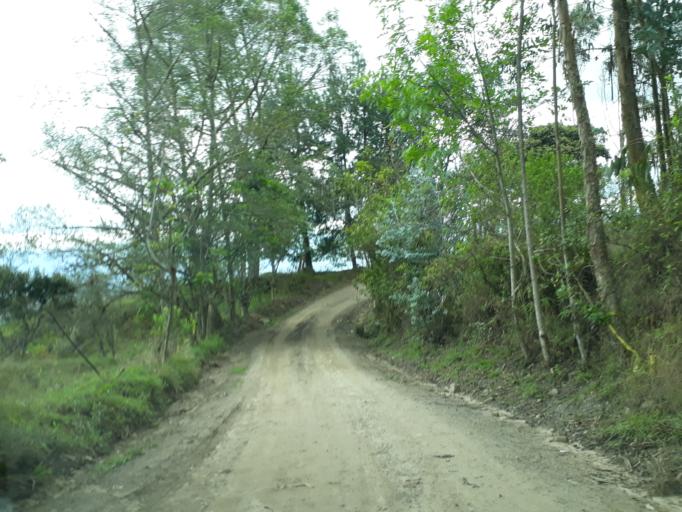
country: CO
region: Cundinamarca
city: Manta
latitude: 5.0233
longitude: -73.5404
